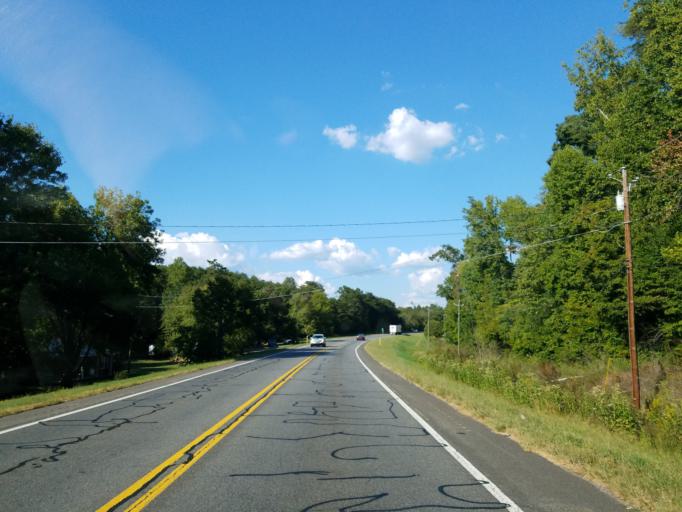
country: US
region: Georgia
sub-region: Bartow County
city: Rydal
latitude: 34.3515
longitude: -84.7230
